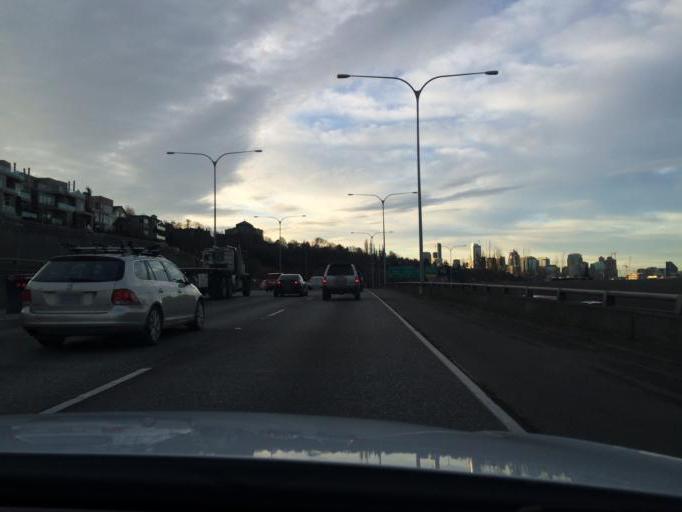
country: US
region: Washington
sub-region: King County
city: Seattle
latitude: 47.6386
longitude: -122.3231
